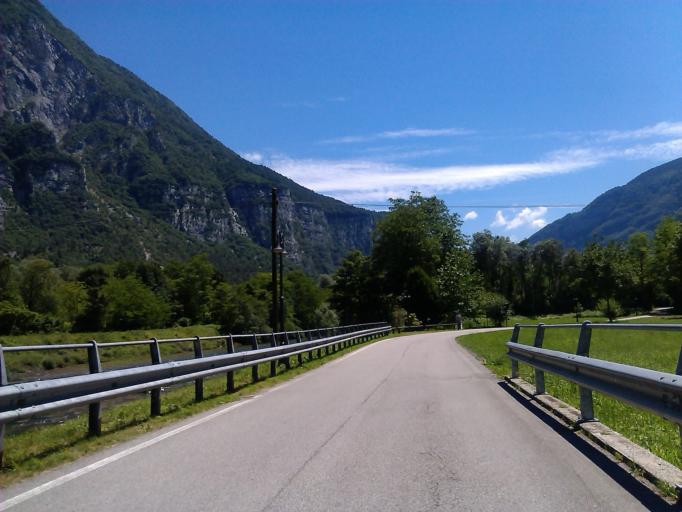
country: IT
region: Trentino-Alto Adige
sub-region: Provincia di Trento
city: Grigno
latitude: 45.9890
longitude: 11.6661
